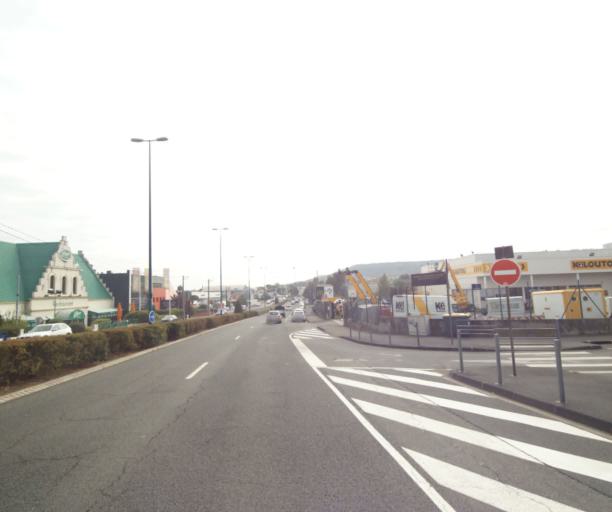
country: FR
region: Auvergne
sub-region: Departement du Puy-de-Dome
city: Aubiere
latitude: 45.7677
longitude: 3.1247
